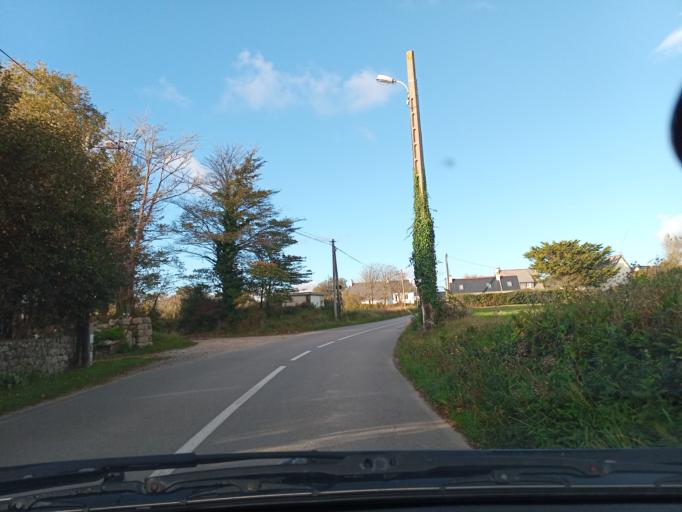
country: FR
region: Brittany
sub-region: Departement du Finistere
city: Esquibien
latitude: 48.0183
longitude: -4.5648
